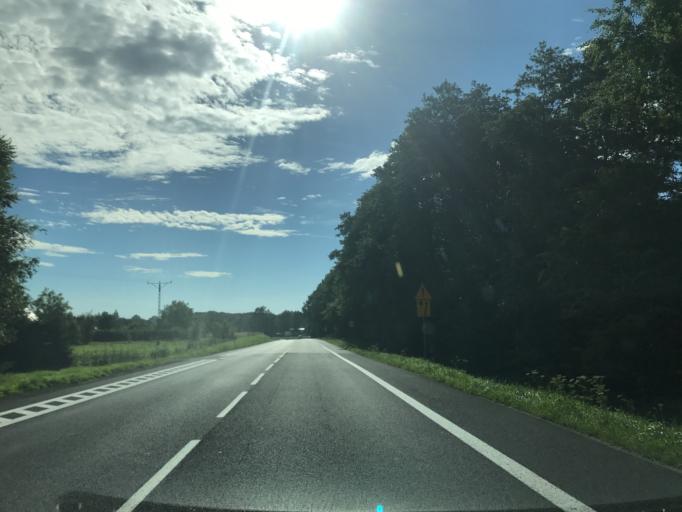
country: PL
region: West Pomeranian Voivodeship
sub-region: Powiat slawienski
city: Darlowo
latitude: 54.2778
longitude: 16.4692
